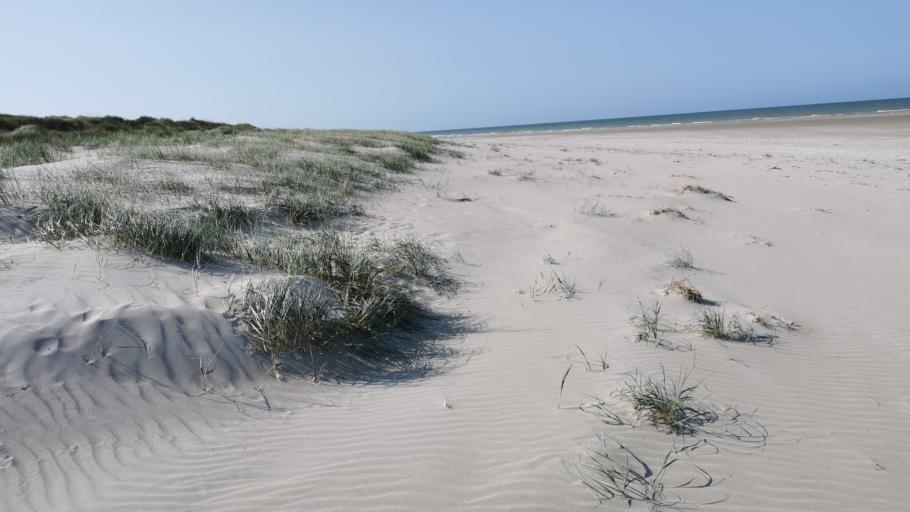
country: FR
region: Picardie
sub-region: Departement de la Somme
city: Fort-Mahon-Plage
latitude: 50.3639
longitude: 1.5547
